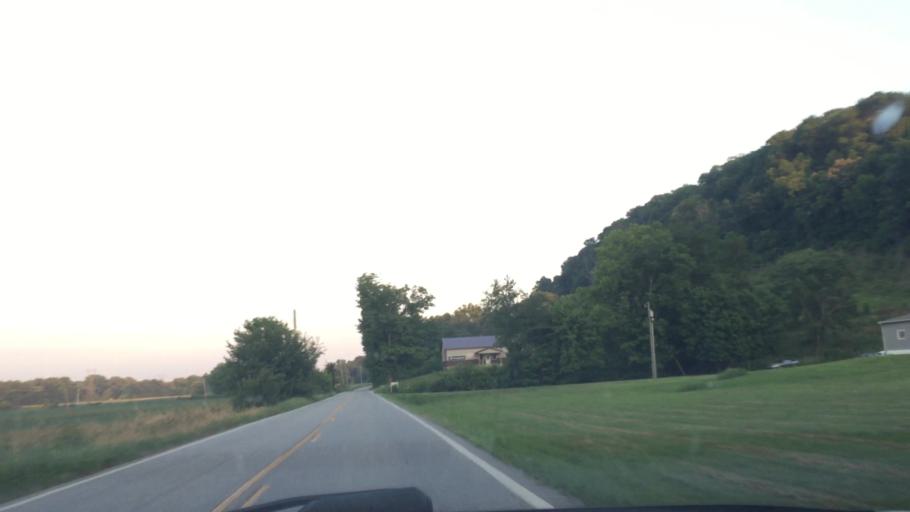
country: US
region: Kentucky
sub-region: Carroll County
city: Carrollton
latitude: 38.6738
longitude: -85.1958
